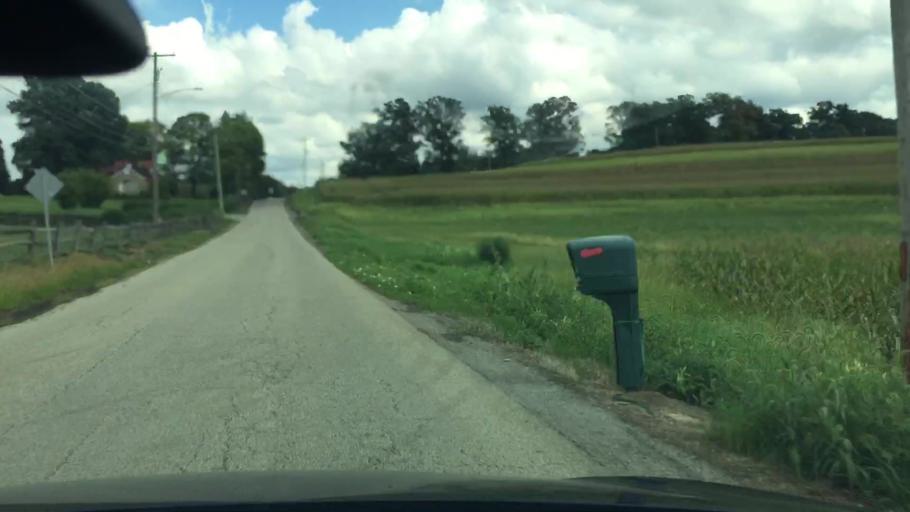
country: US
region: Pennsylvania
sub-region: Butler County
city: Meadowood
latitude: 40.8359
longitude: -79.8796
